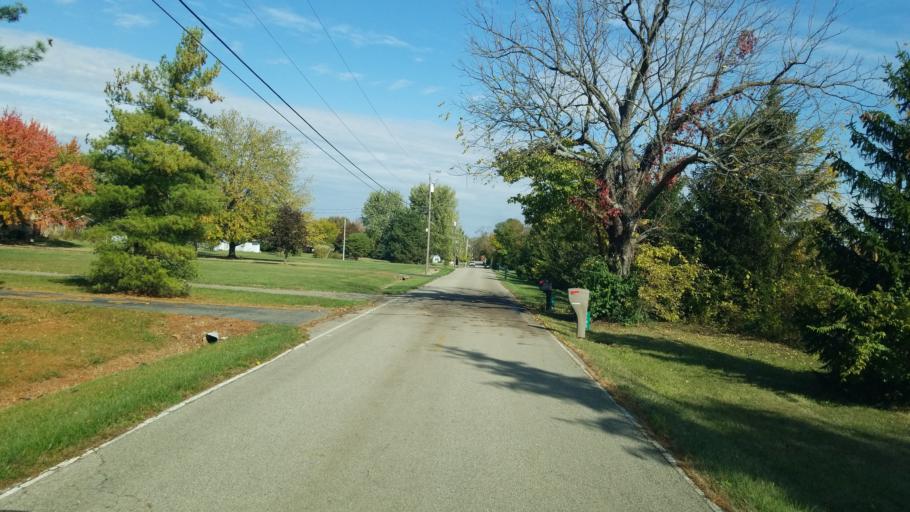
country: US
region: Ohio
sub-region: Warren County
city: Lebanon
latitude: 39.4143
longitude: -84.1699
